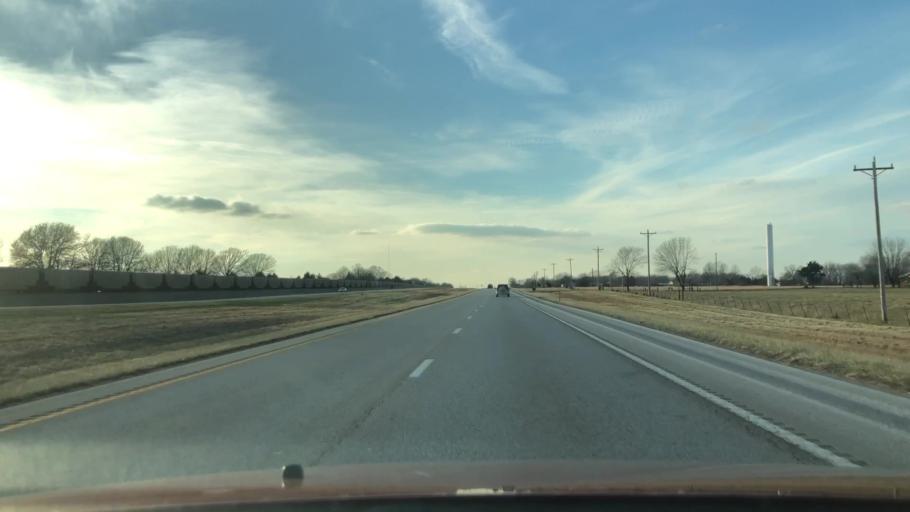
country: US
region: Missouri
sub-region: Webster County
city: Seymour
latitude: 37.1710
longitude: -92.8384
